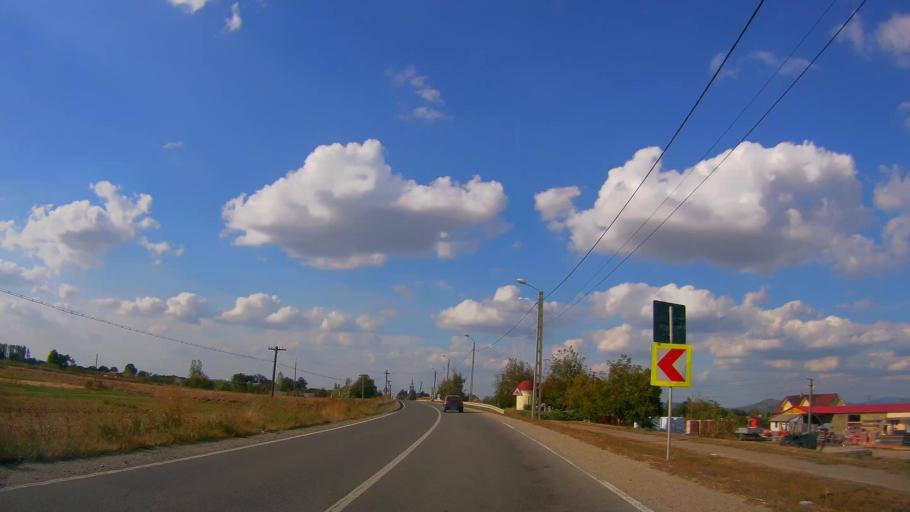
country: RO
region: Satu Mare
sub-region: Comuna Turulung
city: Turulung
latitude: 47.9296
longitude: 23.0849
